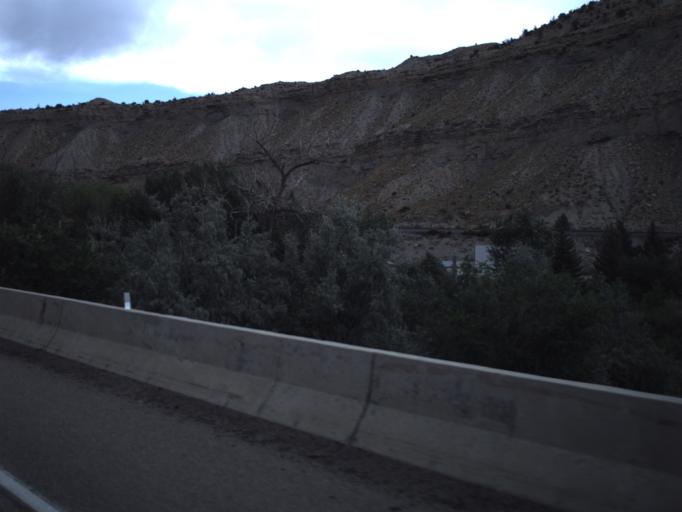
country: US
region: Utah
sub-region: Carbon County
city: Spring Glen
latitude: 39.6389
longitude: -110.8598
